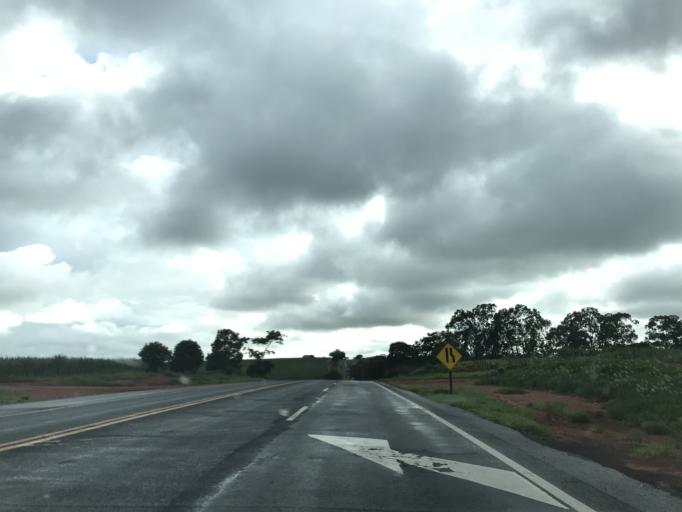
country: BR
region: Sao Paulo
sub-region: Penapolis
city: Penapolis
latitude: -21.4978
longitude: -50.2476
